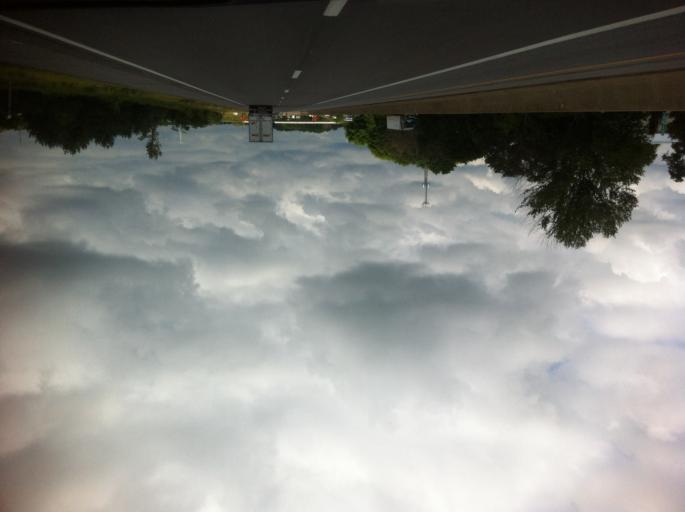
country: US
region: Ohio
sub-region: Trumbull County
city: Lordstown
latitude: 41.1439
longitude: -80.8808
